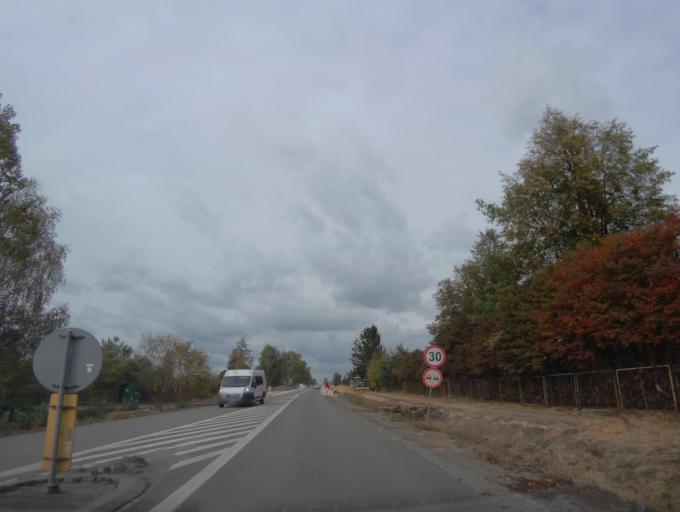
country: PL
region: Lublin Voivodeship
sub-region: Powiat wlodawski
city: Wlodawa
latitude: 51.5508
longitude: 23.5369
